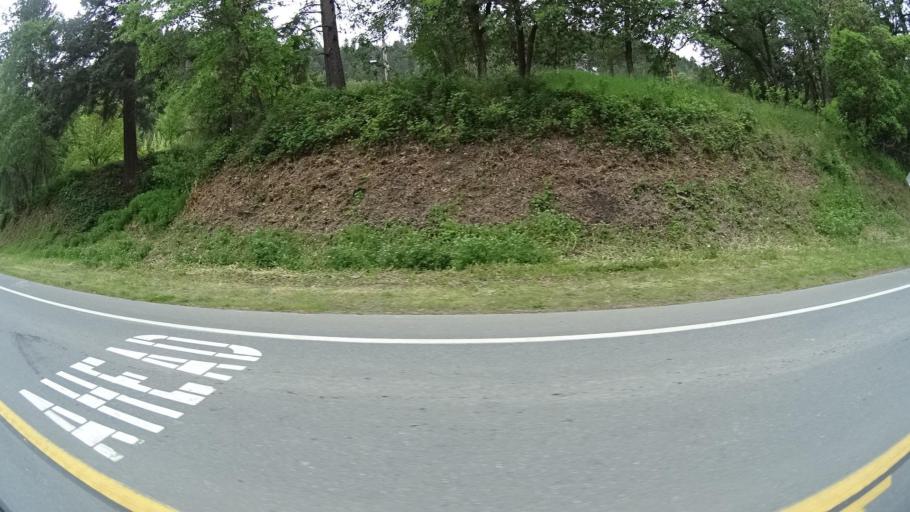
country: US
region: California
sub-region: Humboldt County
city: Willow Creek
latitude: 40.9405
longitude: -123.6314
